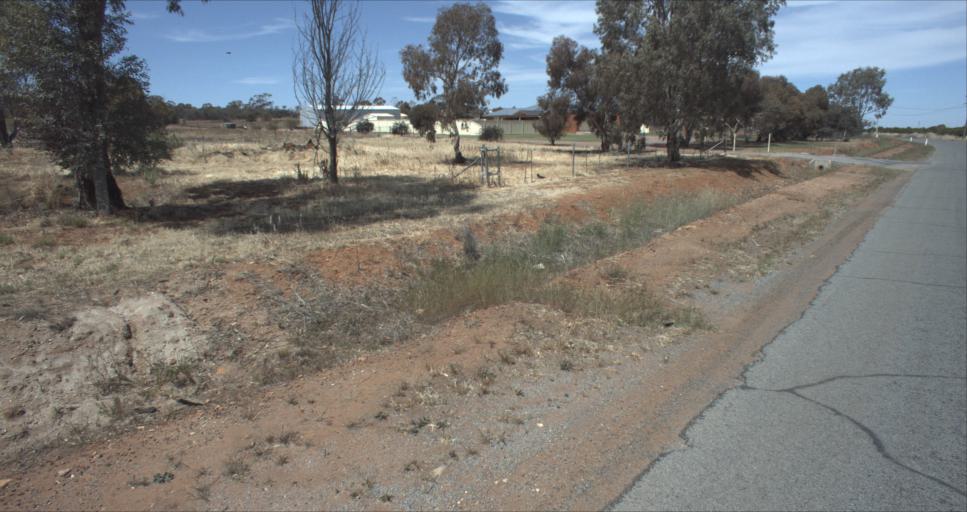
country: AU
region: New South Wales
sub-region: Leeton
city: Leeton
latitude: -34.5820
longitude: 146.4273
